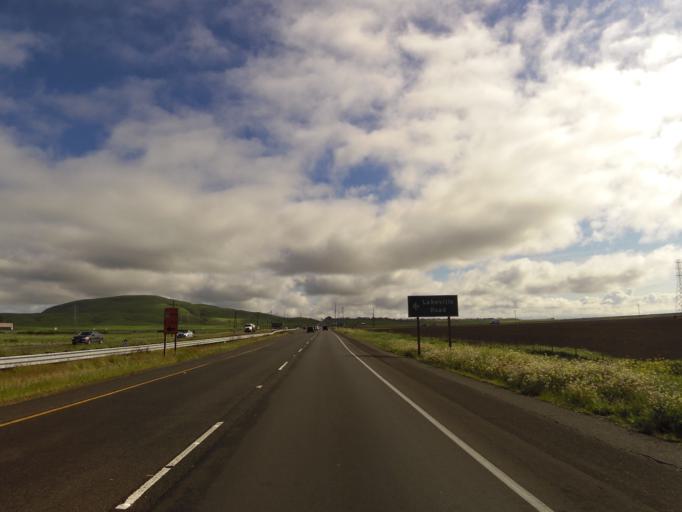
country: US
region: California
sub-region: Marin County
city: Black Point-Green Point
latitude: 38.1322
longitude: -122.4792
